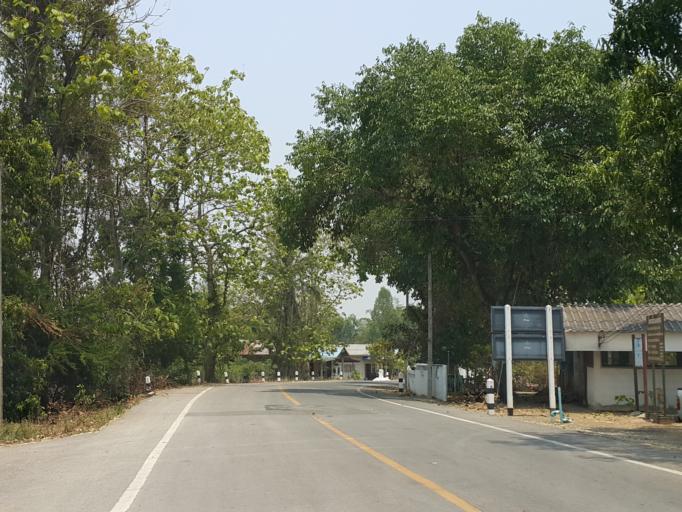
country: TH
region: Kamphaeng Phet
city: Pang Sila Thong
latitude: 16.0548
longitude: 99.3496
